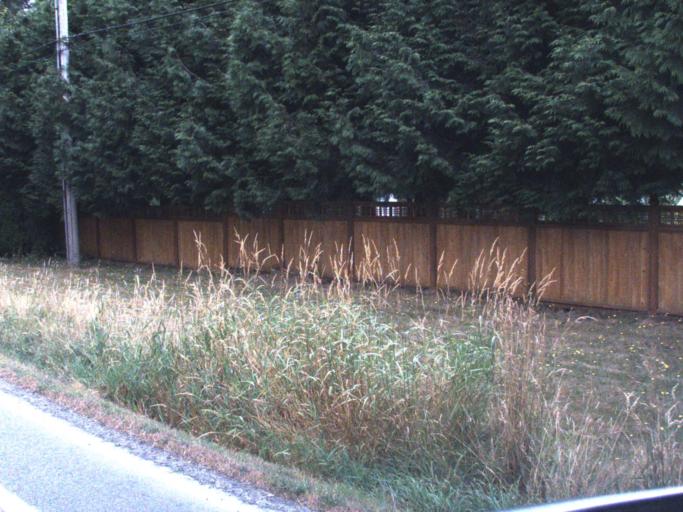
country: US
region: Washington
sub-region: King County
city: Fall City
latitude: 47.5734
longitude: -121.9142
